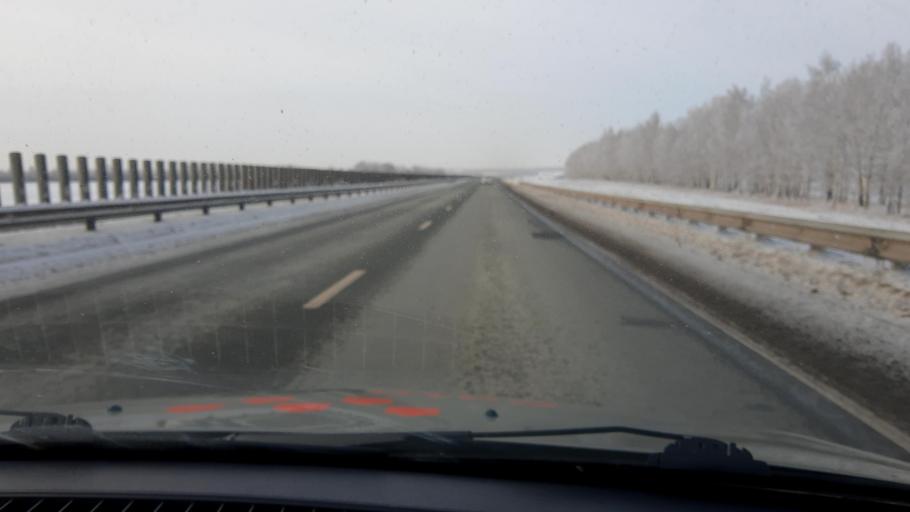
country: RU
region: Bashkortostan
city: Dmitriyevka
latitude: 54.6750
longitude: 55.3603
